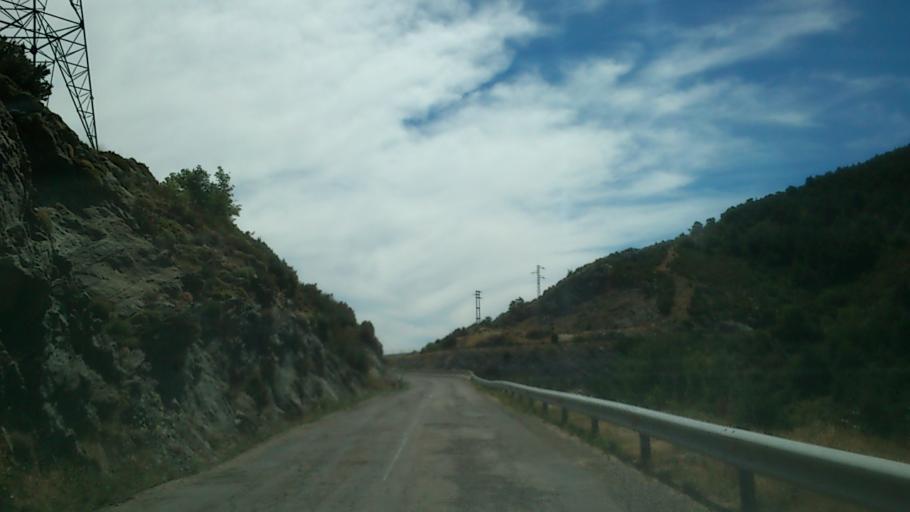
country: ES
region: Aragon
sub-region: Provincia de Huesca
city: Arguis
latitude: 42.3266
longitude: -0.4141
